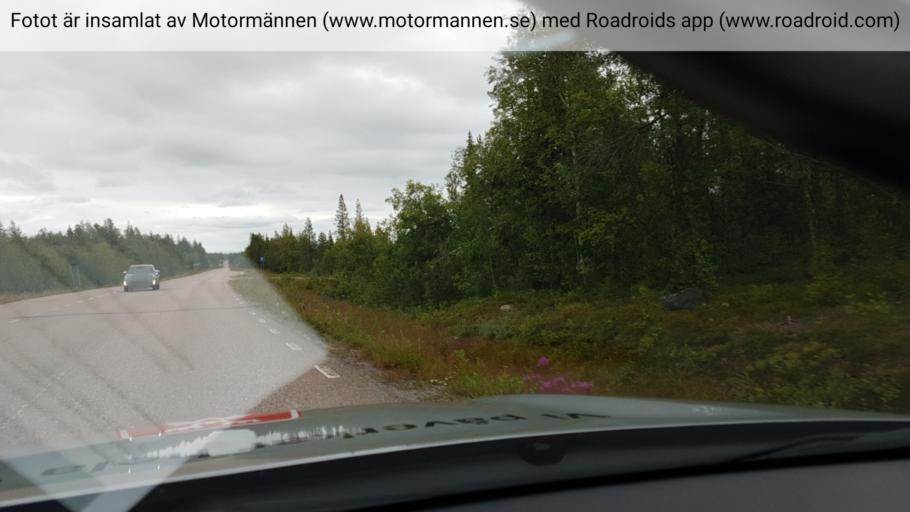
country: SE
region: Norrbotten
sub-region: Overkalix Kommun
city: OEverkalix
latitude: 67.0451
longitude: 22.0654
